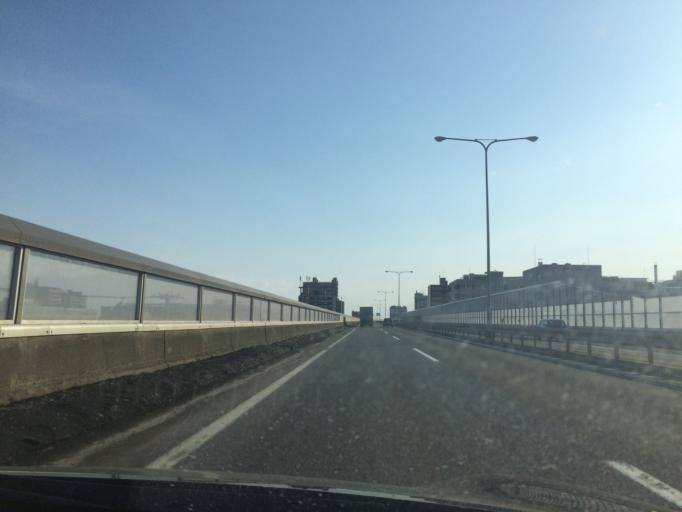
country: JP
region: Hokkaido
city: Sapporo
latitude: 43.1037
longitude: 141.3625
